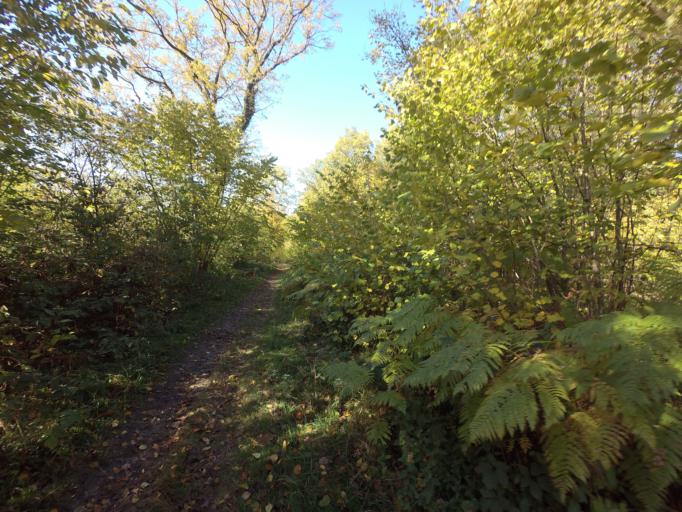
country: BE
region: Wallonia
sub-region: Province de Liege
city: Plombieres
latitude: 50.7717
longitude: 5.9329
